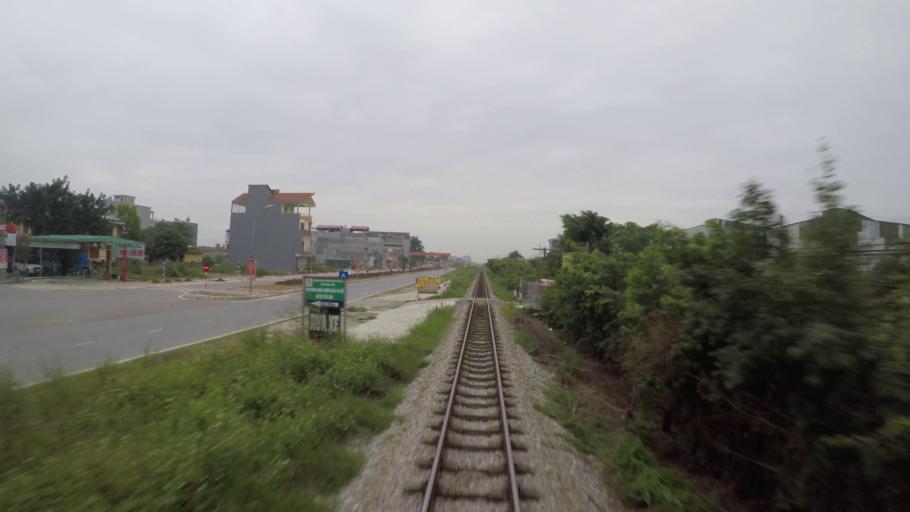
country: VN
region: Hung Yen
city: Nhu Quynh
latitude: 20.9803
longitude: 106.0209
